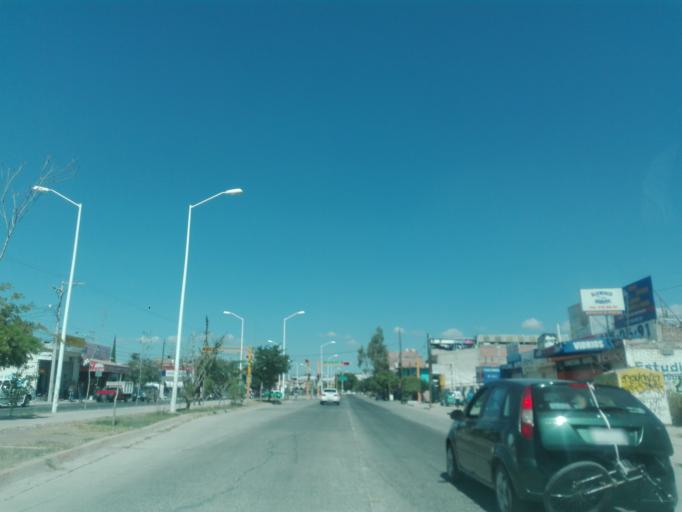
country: MX
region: Guanajuato
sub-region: Leon
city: San Jose de Duran (Los Troncoso)
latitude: 21.0725
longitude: -101.6364
